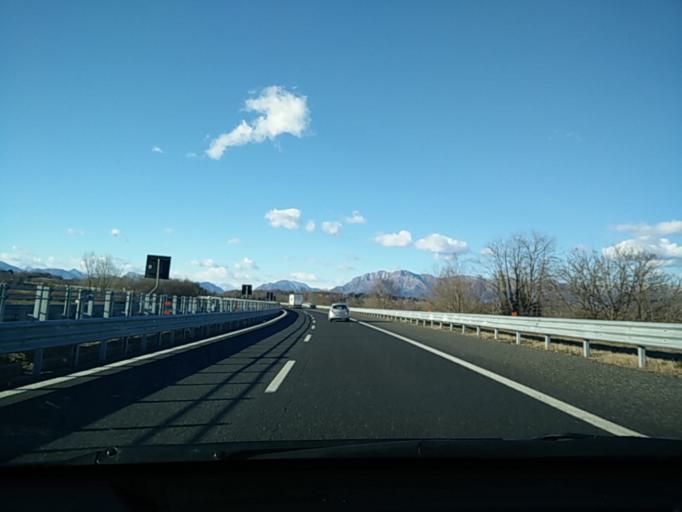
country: IT
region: Friuli Venezia Giulia
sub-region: Provincia di Udine
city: Tavagnacco
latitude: 46.1227
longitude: 13.2047
